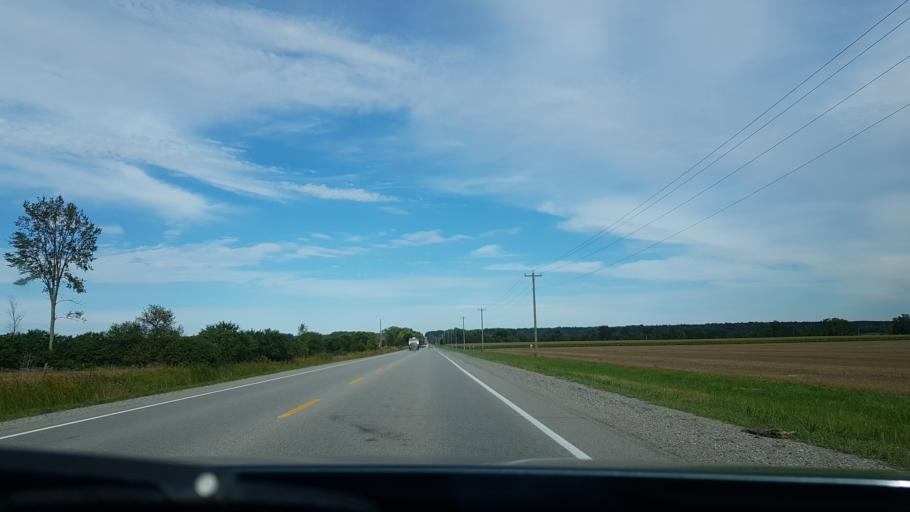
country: CA
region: Ontario
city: Angus
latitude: 44.4706
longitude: -79.8560
